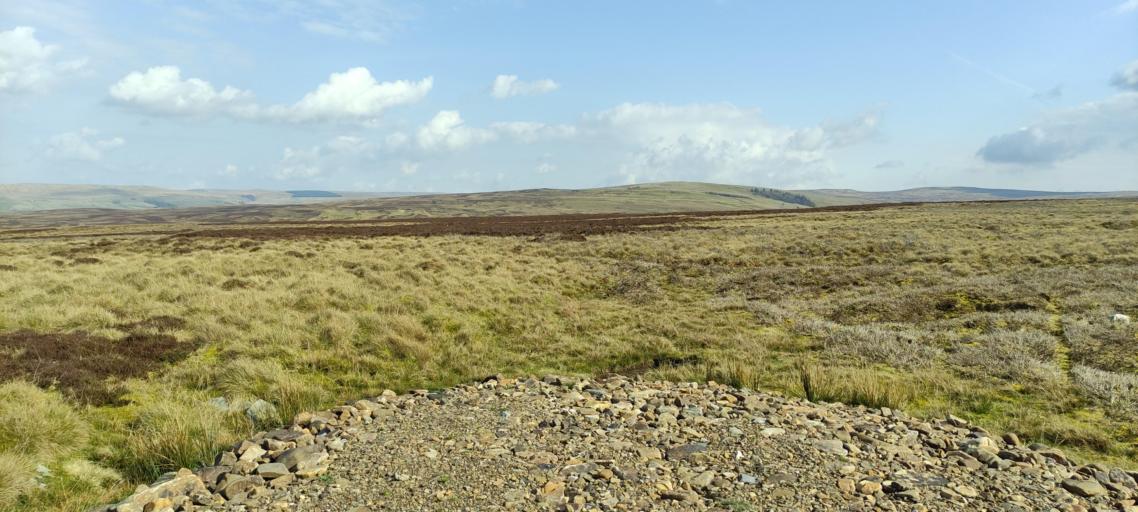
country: GB
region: England
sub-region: Cumbria
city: Appleby-in-Westmorland
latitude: 54.7584
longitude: -2.5111
